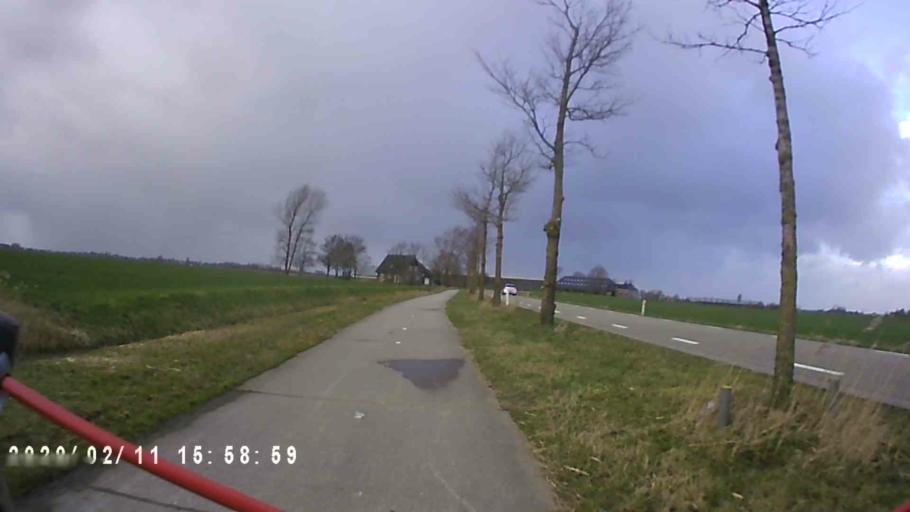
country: NL
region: Groningen
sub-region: Gemeente Zuidhorn
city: Oldehove
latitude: 53.2894
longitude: 6.4220
